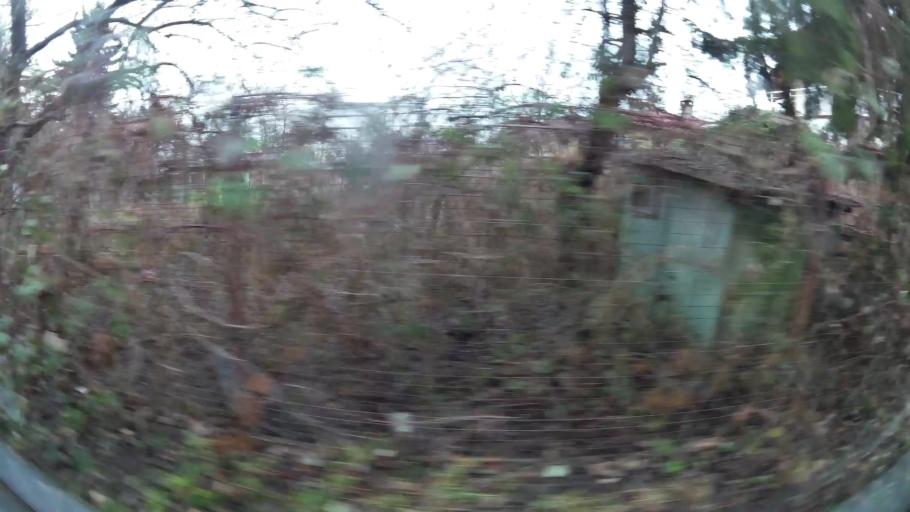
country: BG
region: Sofia-Capital
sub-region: Stolichna Obshtina
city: Sofia
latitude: 42.6155
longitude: 23.3696
